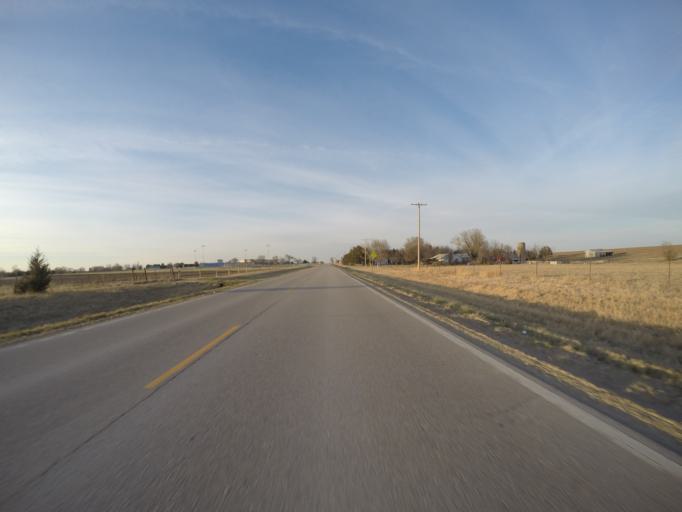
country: US
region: Kansas
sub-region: Riley County
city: Fort Riley North
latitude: 39.3301
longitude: -96.8307
